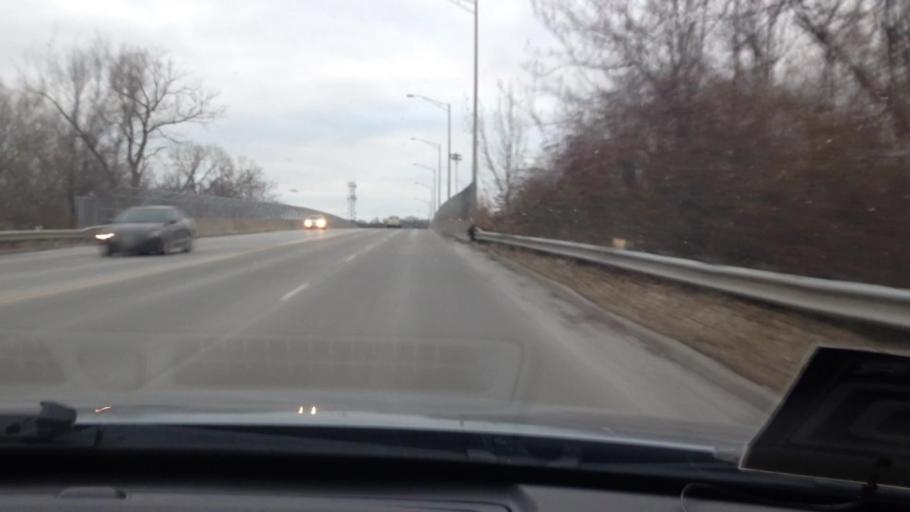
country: US
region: Missouri
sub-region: Clay County
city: North Kansas City
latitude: 39.1258
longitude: -94.5186
